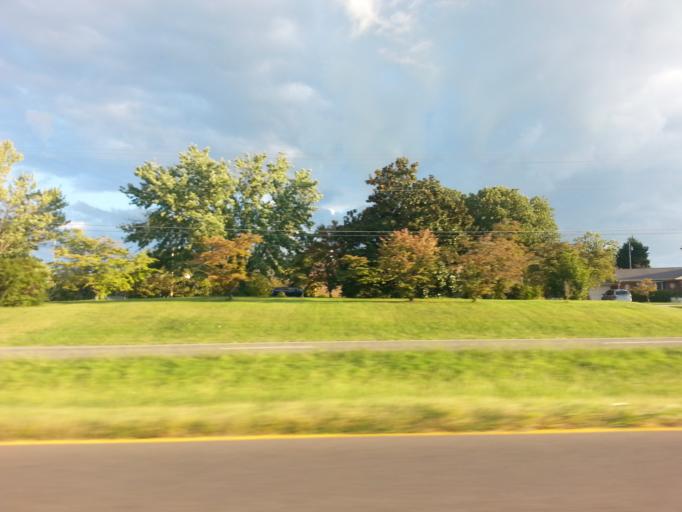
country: US
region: Tennessee
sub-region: Jefferson County
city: New Market
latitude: 36.1077
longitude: -83.5245
